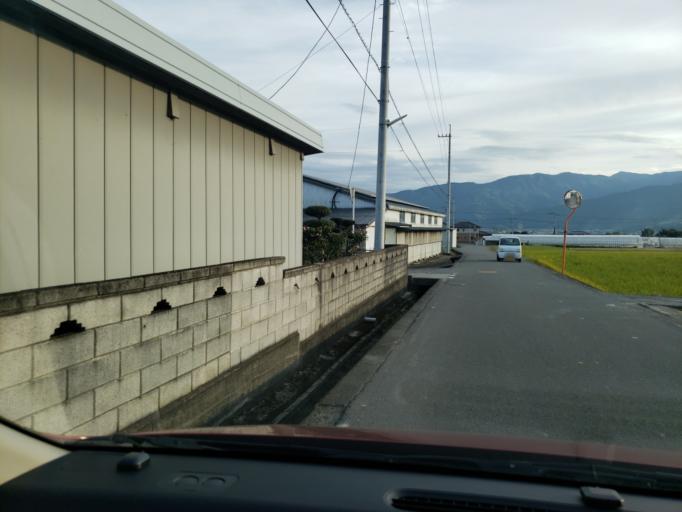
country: JP
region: Tokushima
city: Wakimachi
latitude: 34.0847
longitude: 134.2269
